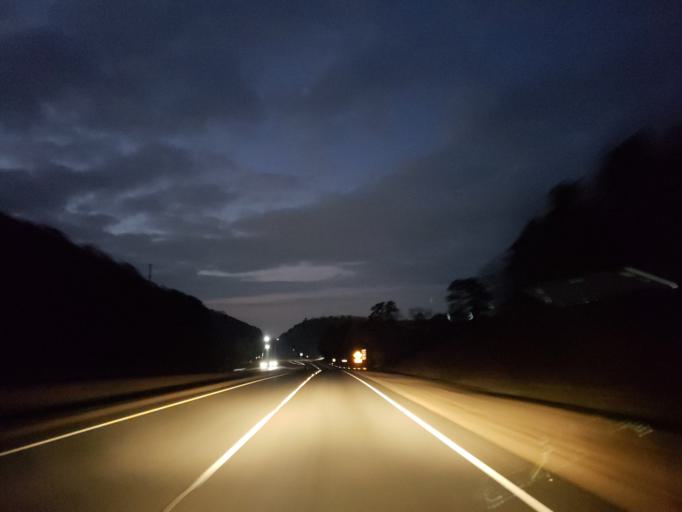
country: US
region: Georgia
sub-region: Polk County
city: Rockmart
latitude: 33.9725
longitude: -85.0022
